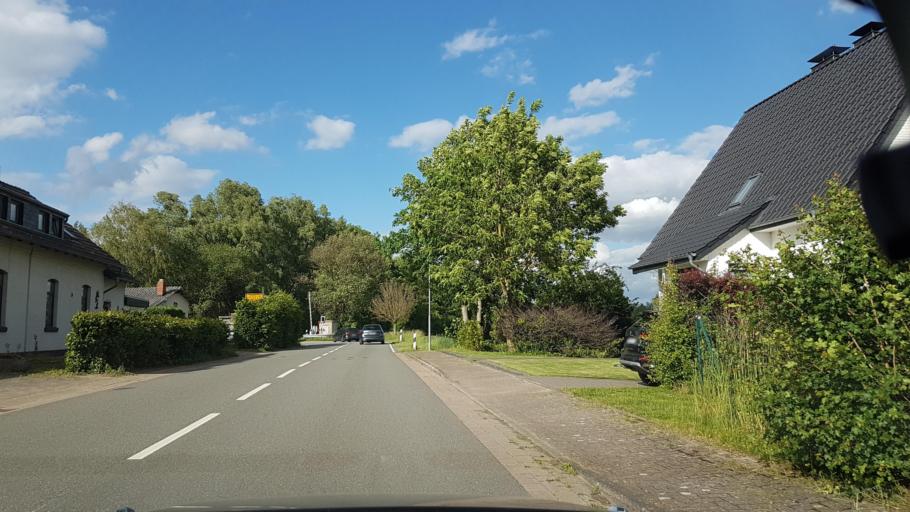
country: DE
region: Lower Saxony
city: Heinsen
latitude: 52.0992
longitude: 9.6721
